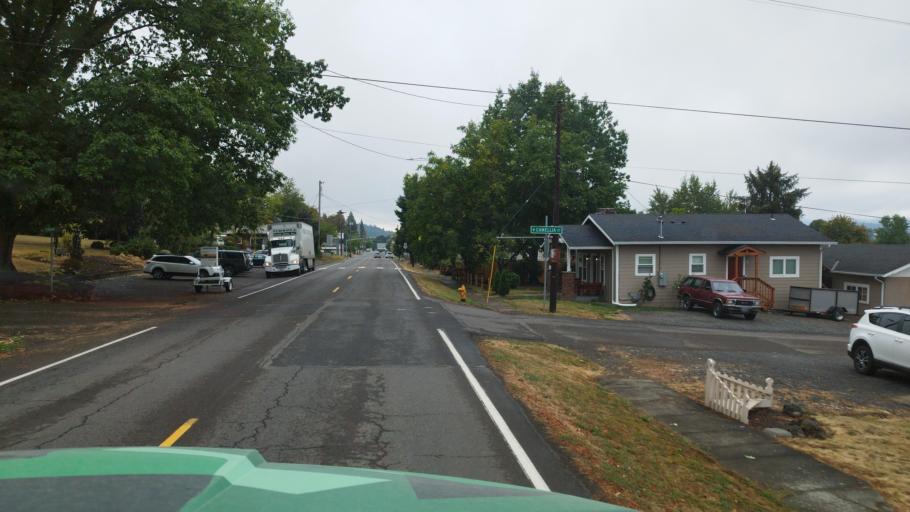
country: US
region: Oregon
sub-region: Yamhill County
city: Yamhill
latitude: 45.3439
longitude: -123.1879
